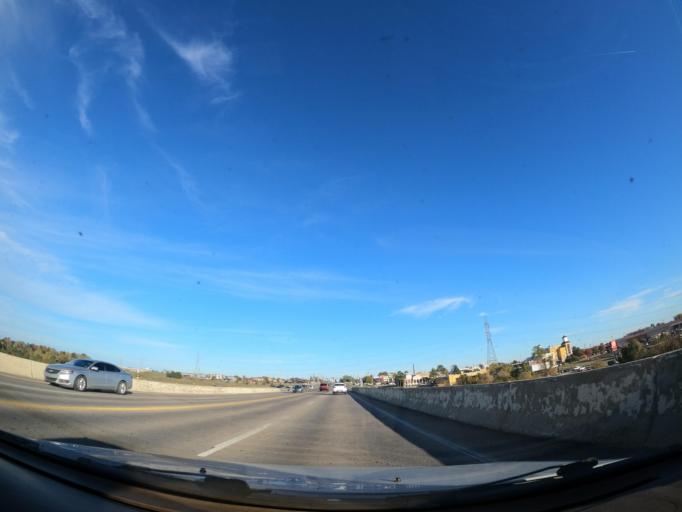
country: US
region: Oklahoma
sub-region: Tulsa County
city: Owasso
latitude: 36.2935
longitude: -95.8348
